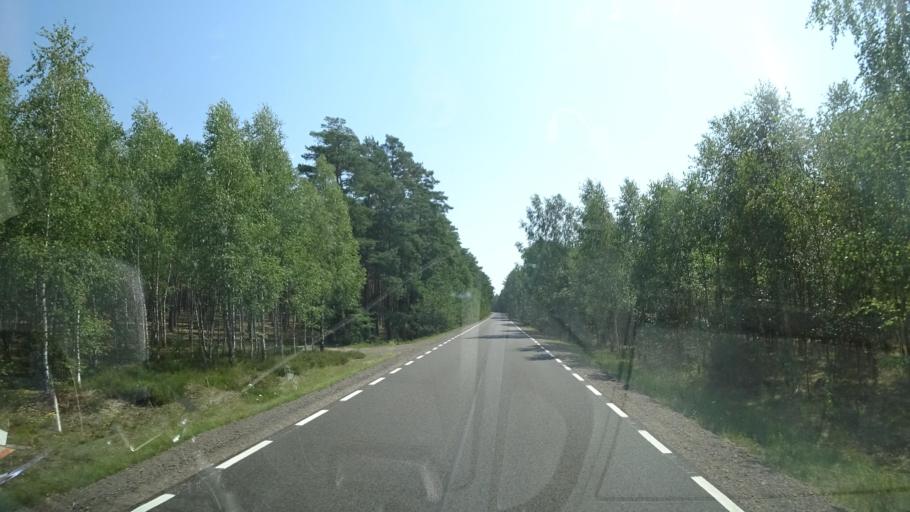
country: PL
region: Pomeranian Voivodeship
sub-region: Powiat chojnicki
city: Chojnice
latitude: 53.8611
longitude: 17.5262
